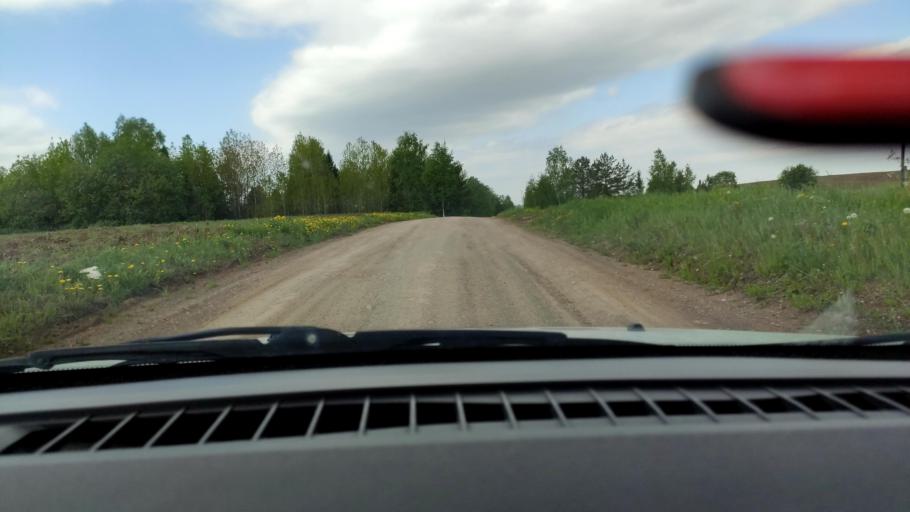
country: RU
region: Perm
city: Bershet'
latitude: 57.7230
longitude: 56.3988
